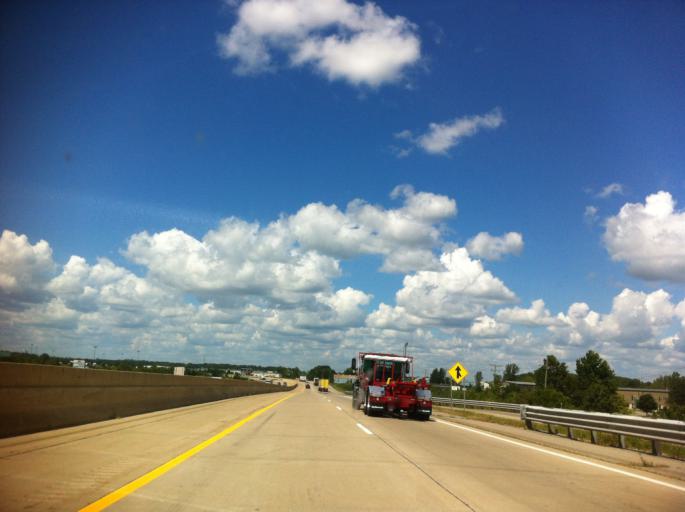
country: US
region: Michigan
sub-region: Monroe County
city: Dundee
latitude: 41.9583
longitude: -83.6723
